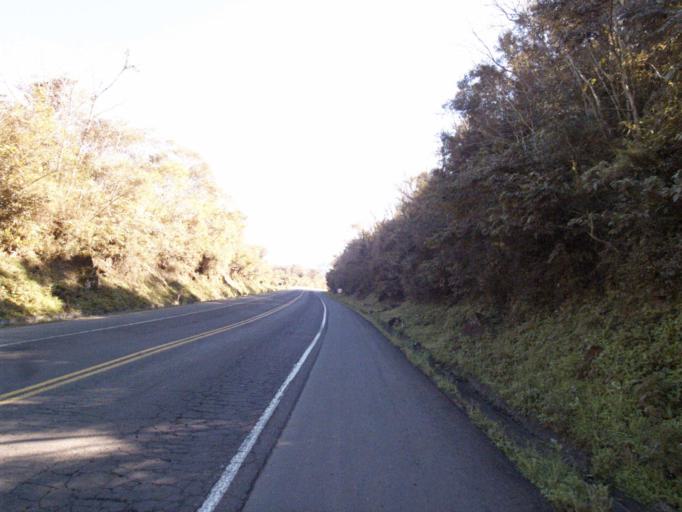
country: BR
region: Rio Grande do Sul
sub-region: Frederico Westphalen
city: Frederico Westphalen
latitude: -26.9992
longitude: -53.2267
